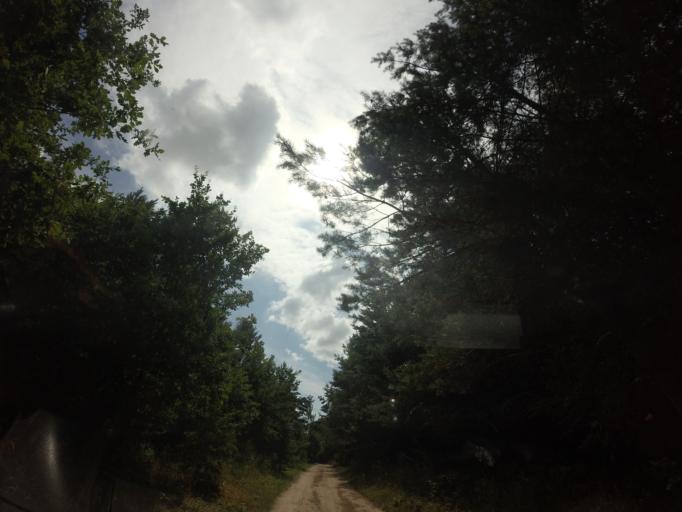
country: PL
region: West Pomeranian Voivodeship
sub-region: Powiat choszczenski
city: Drawno
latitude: 53.1979
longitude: 15.7699
